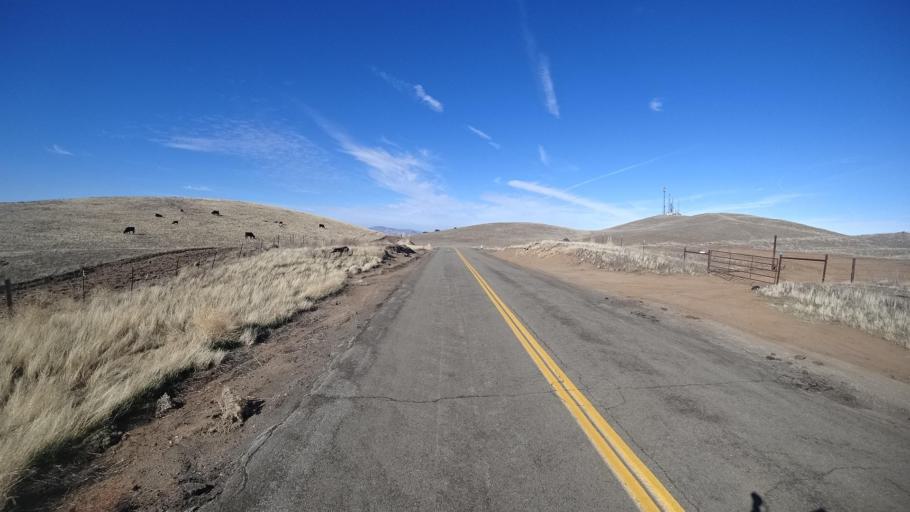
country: US
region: California
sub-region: Kern County
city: Maricopa
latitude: 34.9152
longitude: -119.4030
